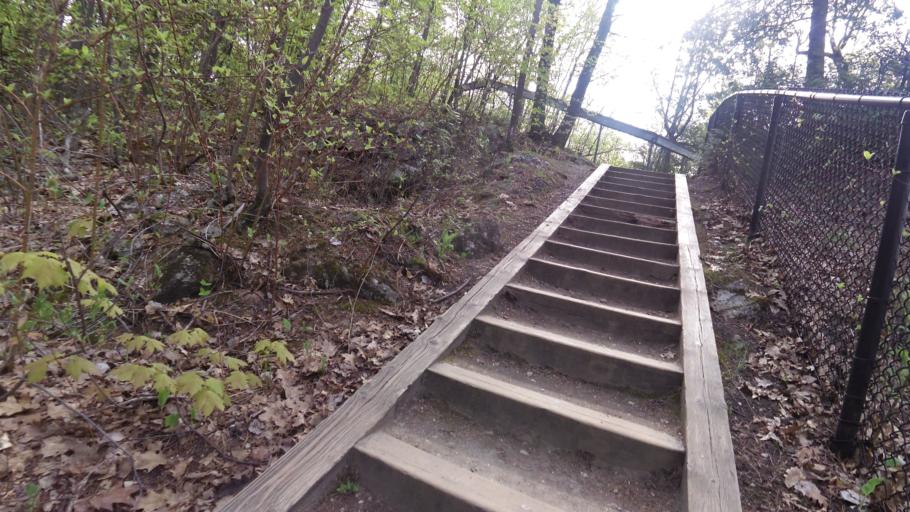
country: CA
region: Quebec
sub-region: Outaouais
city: Gatineau
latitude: 45.4693
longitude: -75.8061
